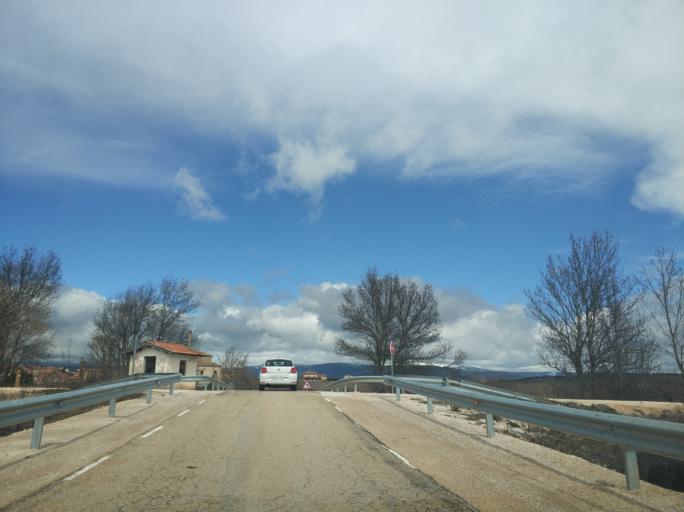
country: ES
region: Castille and Leon
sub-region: Provincia de Soria
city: Abejar
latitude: 41.8017
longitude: -2.7813
